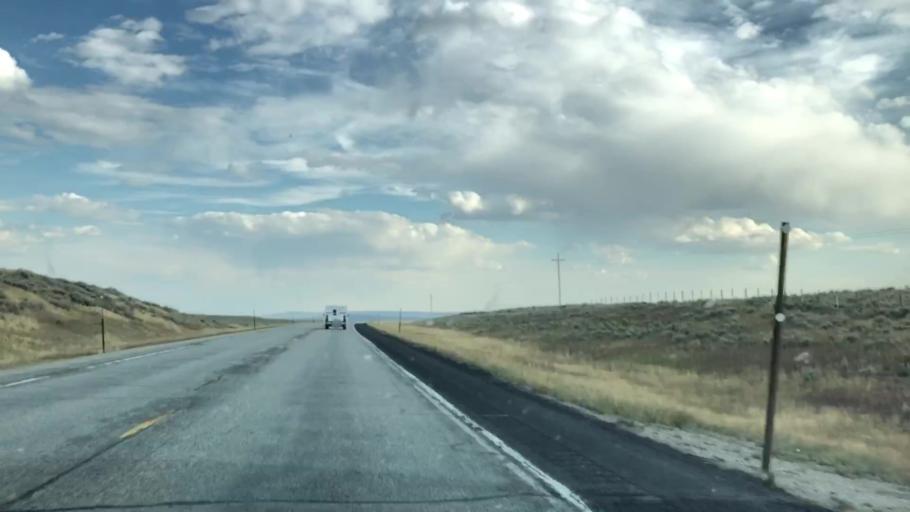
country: US
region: Wyoming
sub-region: Sublette County
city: Pinedale
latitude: 43.0571
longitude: -110.1566
